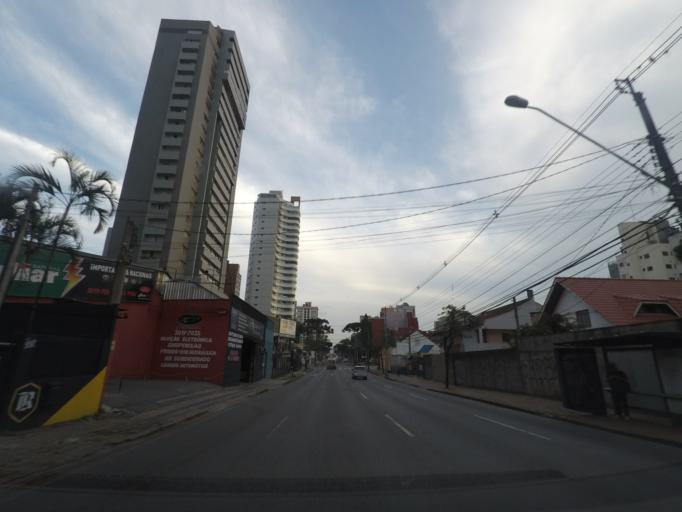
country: BR
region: Parana
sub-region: Curitiba
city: Curitiba
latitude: -25.4116
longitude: -49.2584
